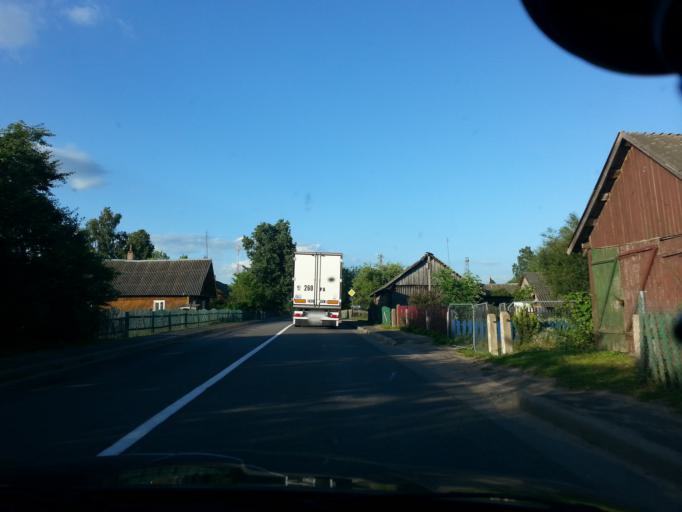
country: BY
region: Minsk
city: Svir
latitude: 54.9182
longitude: 26.4567
